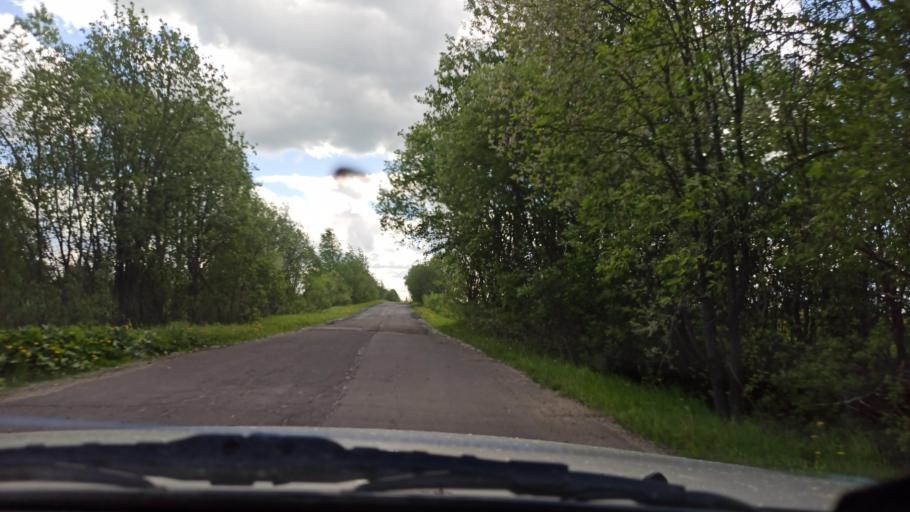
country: RU
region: Vologda
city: Molochnoye
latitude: 59.3759
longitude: 39.7117
